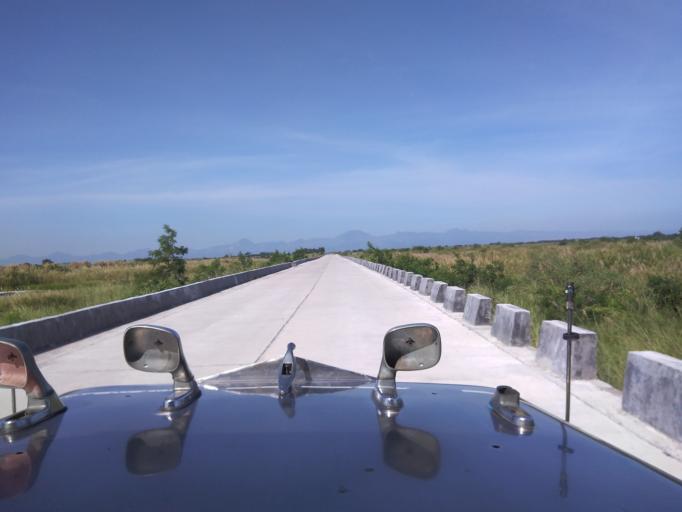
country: PH
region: Central Luzon
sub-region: Province of Pampanga
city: Minalin
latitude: 14.9892
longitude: 120.6820
